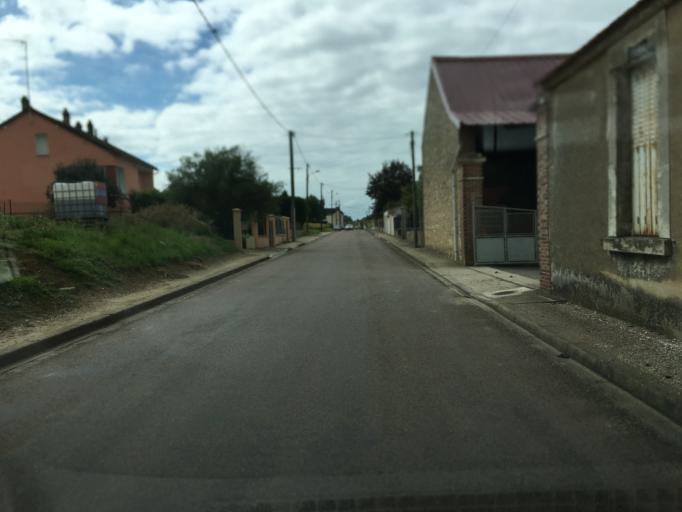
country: FR
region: Bourgogne
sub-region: Departement de l'Yonne
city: Laroche-Saint-Cydroine
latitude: 47.9501
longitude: 3.4429
